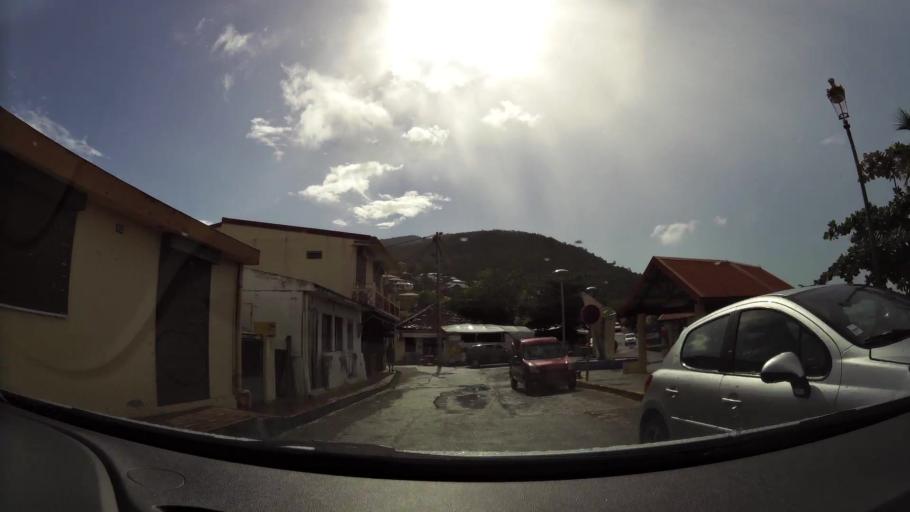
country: MQ
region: Martinique
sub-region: Martinique
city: Les Trois-Ilets
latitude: 14.4897
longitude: -61.0796
